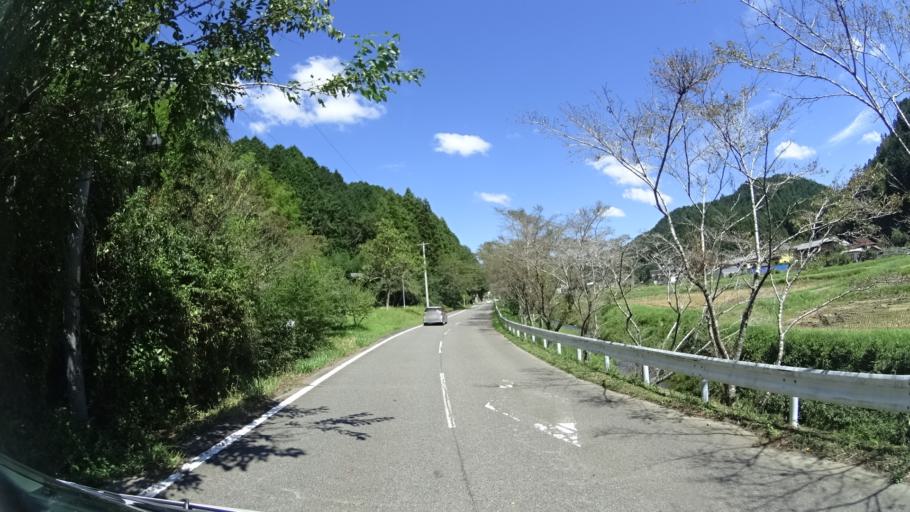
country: JP
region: Gifu
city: Minokamo
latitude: 35.5856
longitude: 137.0845
